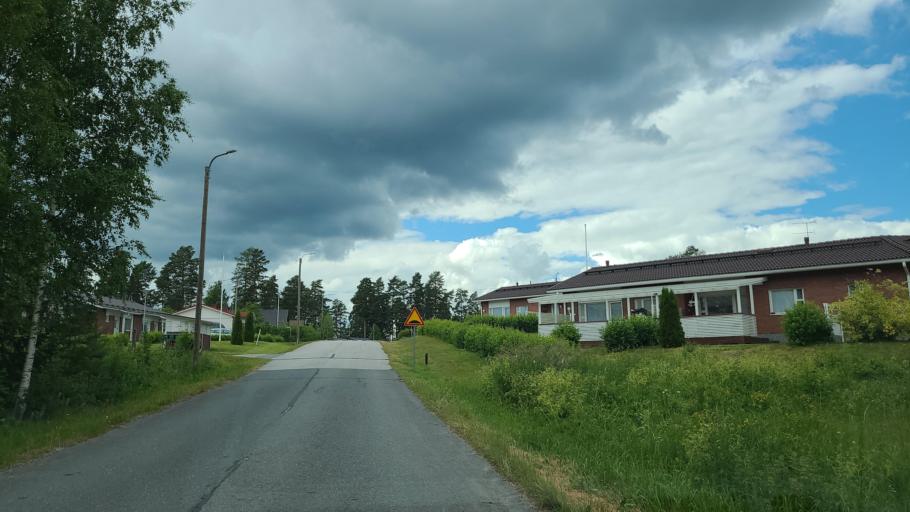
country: FI
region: Northern Savo
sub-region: Koillis-Savo
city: Kaavi
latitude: 62.9731
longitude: 28.4763
